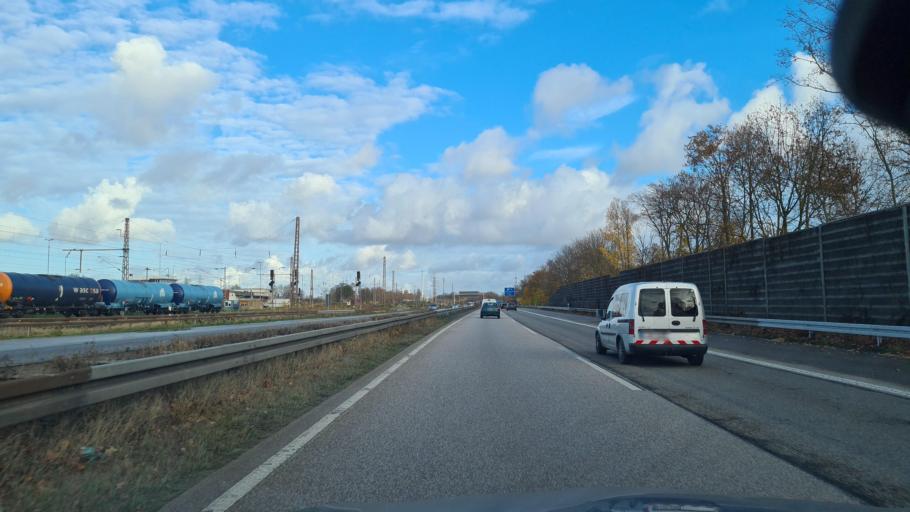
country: DE
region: North Rhine-Westphalia
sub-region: Regierungsbezirk Munster
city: Gelsenkirchen
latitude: 51.5369
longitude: 7.1031
